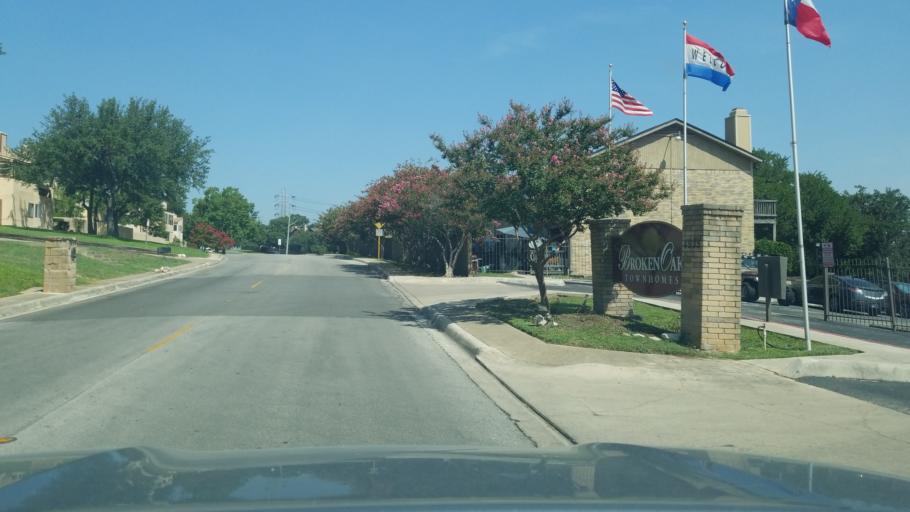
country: US
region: Texas
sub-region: Bexar County
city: Hollywood Park
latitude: 29.5894
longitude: -98.4631
